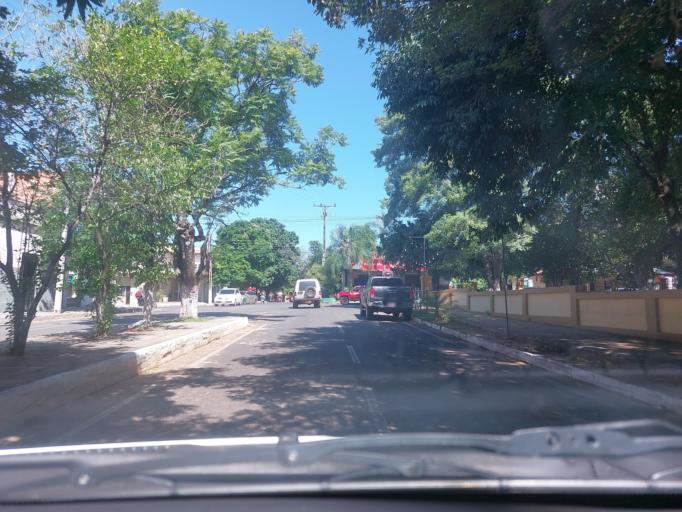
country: PY
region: San Pedro
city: Guayaybi
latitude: -24.6644
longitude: -56.4421
